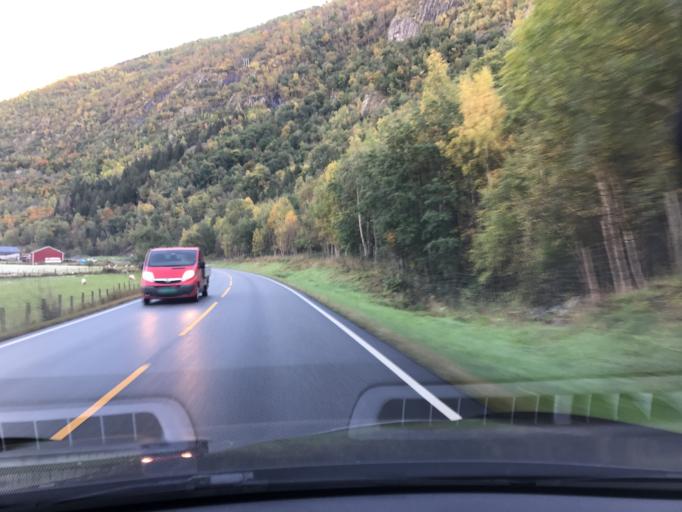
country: NO
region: Sogn og Fjordane
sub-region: Laerdal
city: Laerdalsoyri
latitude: 61.0958
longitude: 7.4807
